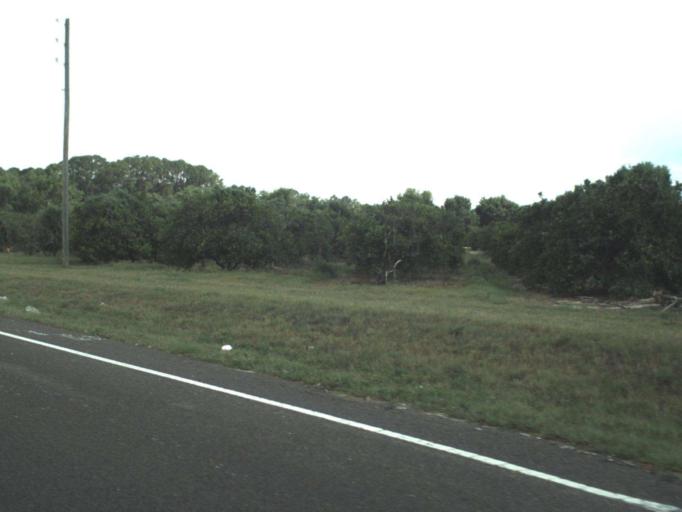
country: US
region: Florida
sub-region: Lake County
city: Mount Dora
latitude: 28.8215
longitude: -81.6350
